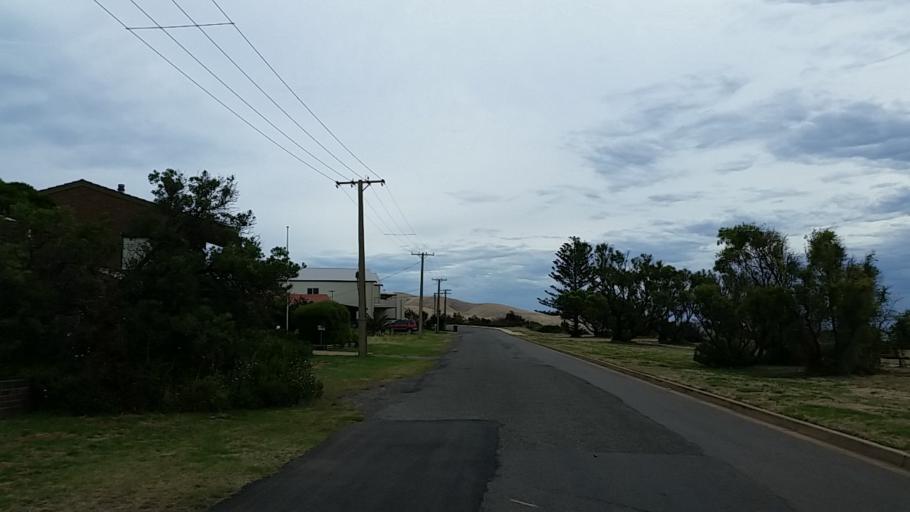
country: AU
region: South Australia
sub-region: Onkaparinga
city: Port Willunga
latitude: -35.3393
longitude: 138.4468
